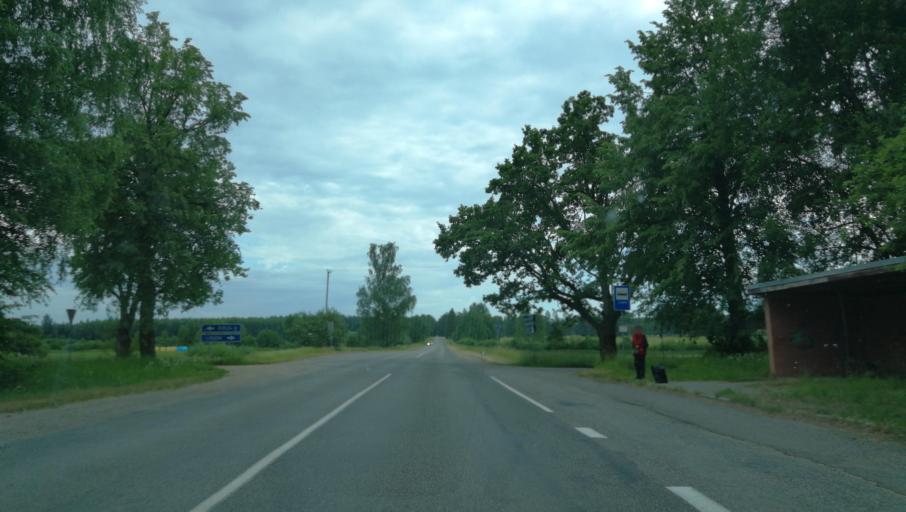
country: LV
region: Valmieras Rajons
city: Valmiera
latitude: 57.6896
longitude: 25.4300
